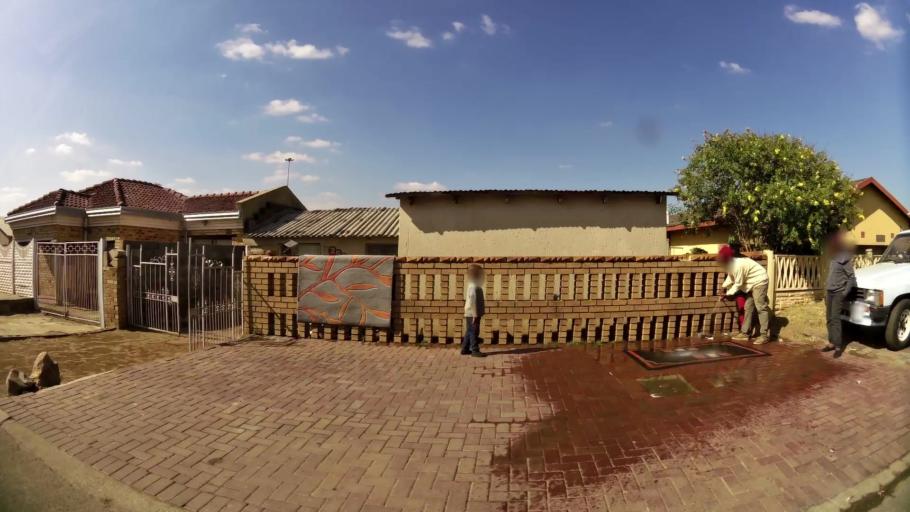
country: ZA
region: Gauteng
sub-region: City of Johannesburg Metropolitan Municipality
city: Soweto
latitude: -26.2539
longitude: 27.8893
